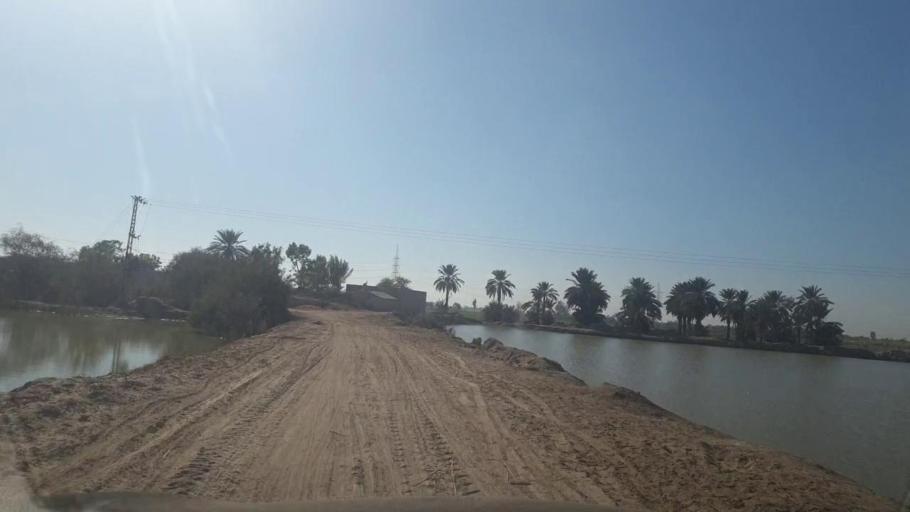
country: PK
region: Sindh
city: Adilpur
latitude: 27.9687
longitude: 69.3435
